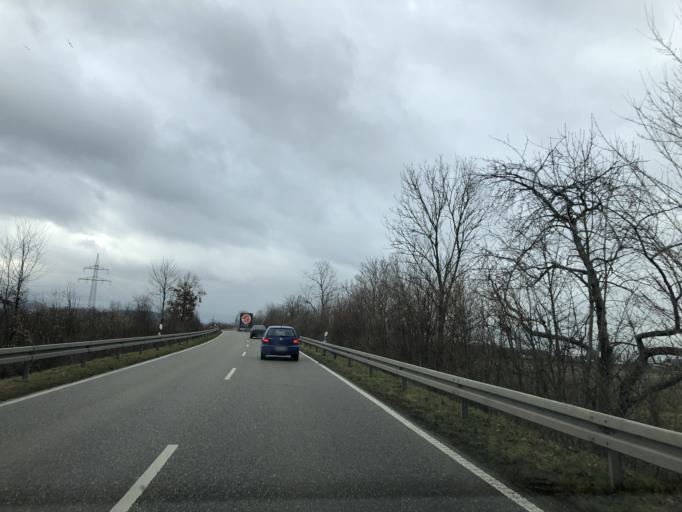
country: DE
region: Baden-Wuerttemberg
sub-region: Karlsruhe Region
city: Muggensturm
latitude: 48.8848
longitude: 8.2978
